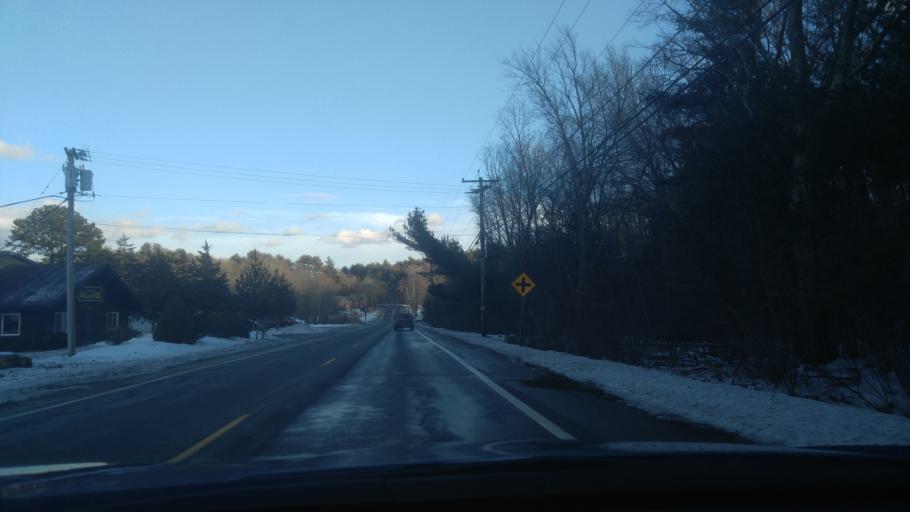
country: US
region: Rhode Island
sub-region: Kent County
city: Coventry
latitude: 41.7030
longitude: -71.6377
